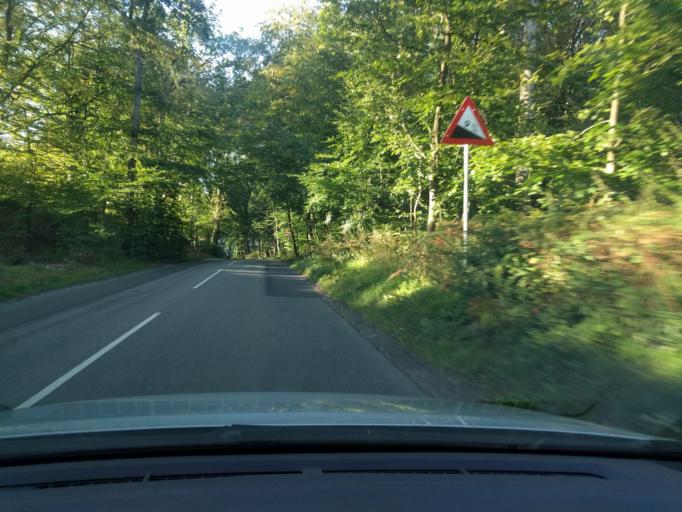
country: DK
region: Central Jutland
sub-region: Skanderborg Kommune
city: Ry
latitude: 56.0945
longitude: 9.7823
